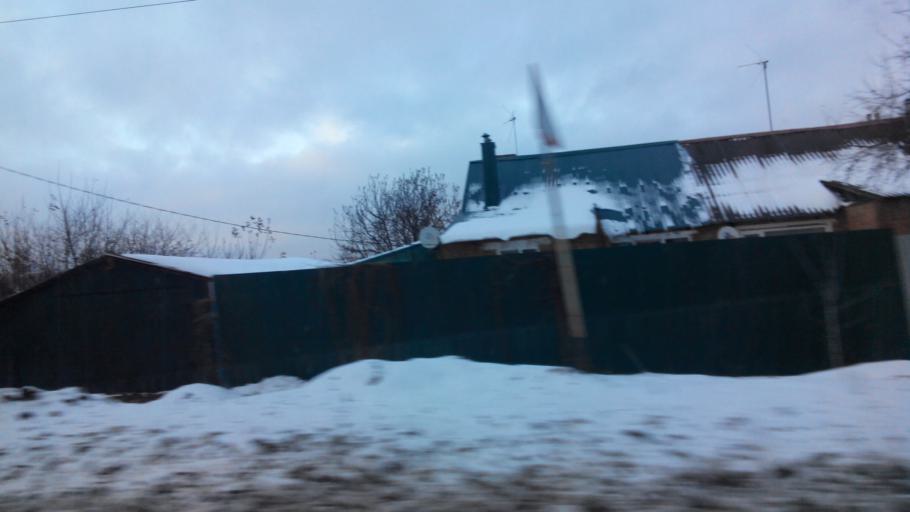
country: RU
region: Tula
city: Podlesnyy
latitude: 53.9648
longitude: 38.2720
